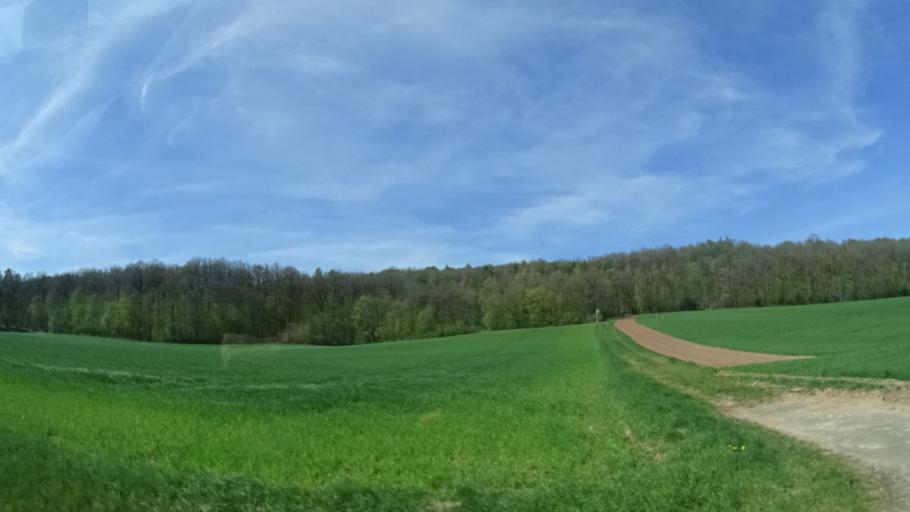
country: DE
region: Bavaria
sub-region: Regierungsbezirk Unterfranken
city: Hofheim in Unterfranken
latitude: 50.1580
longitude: 10.5638
